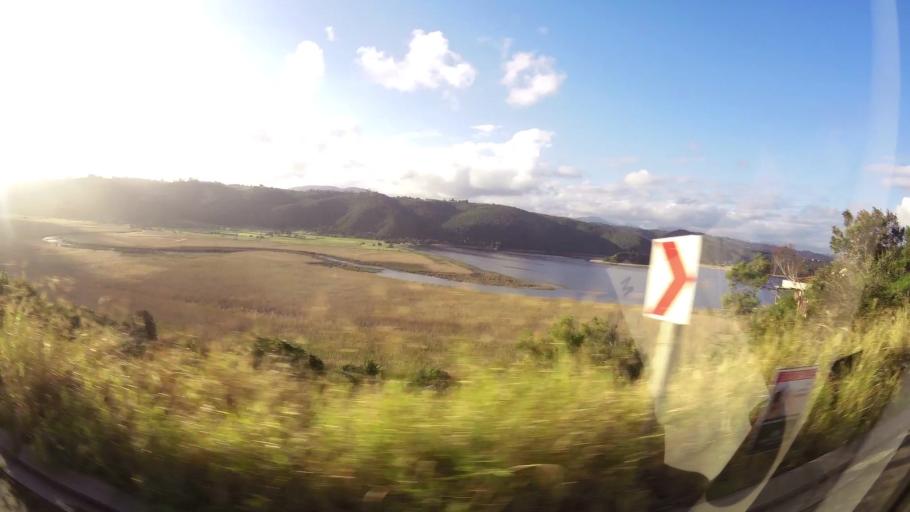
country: ZA
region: Western Cape
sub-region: Eden District Municipality
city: George
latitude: -34.0000
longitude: 22.6334
